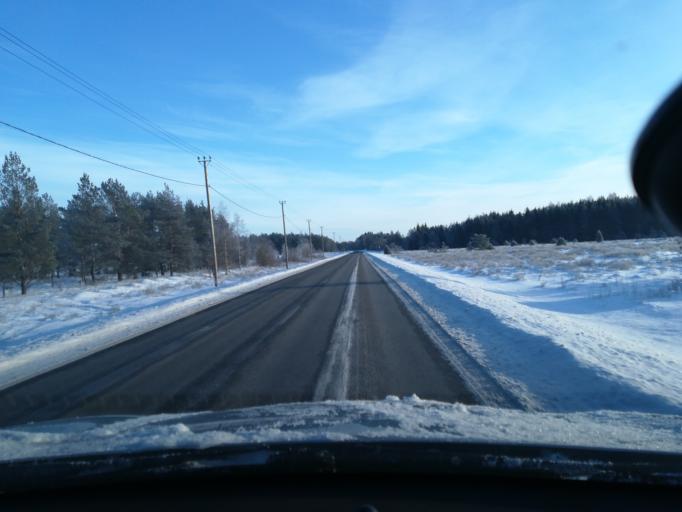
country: EE
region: Harju
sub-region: Keila linn
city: Keila
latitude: 59.3839
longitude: 24.4335
